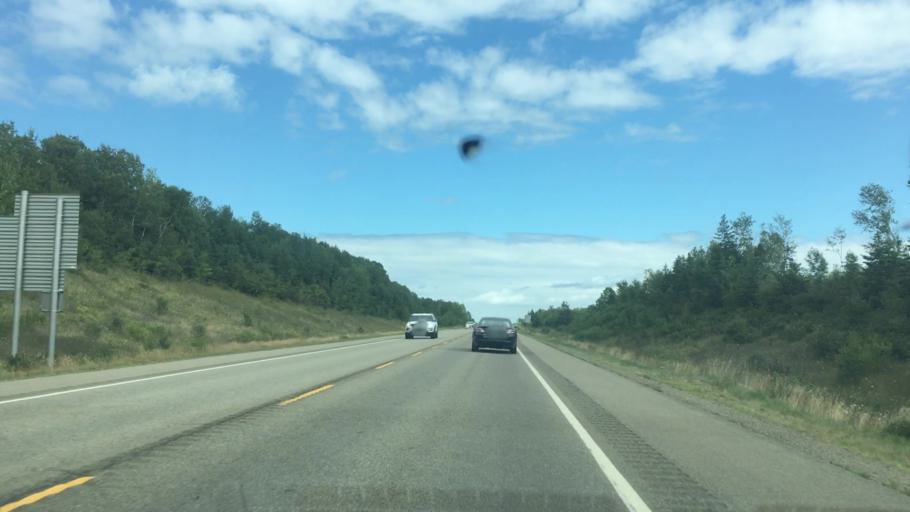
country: CA
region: Nova Scotia
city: Port Hawkesbury
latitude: 45.6202
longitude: -61.6120
